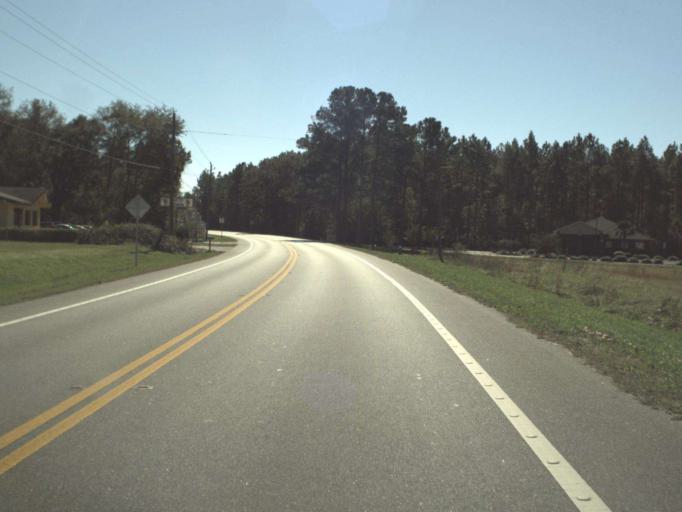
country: US
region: Florida
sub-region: Okaloosa County
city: Crestview
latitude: 30.7882
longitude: -86.6839
